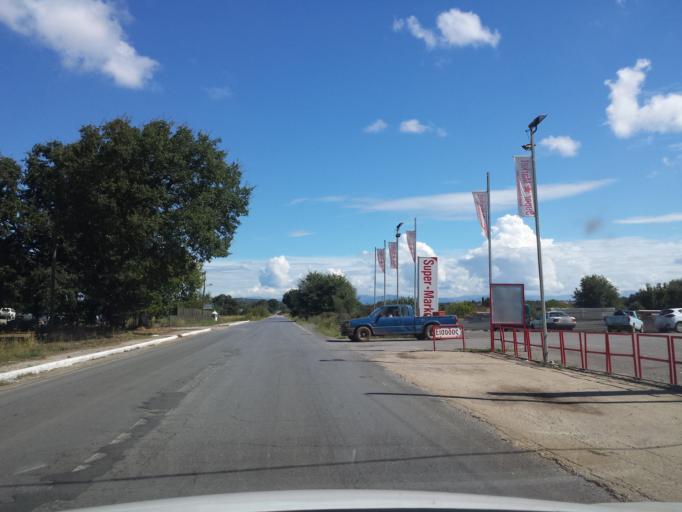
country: GR
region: Peloponnese
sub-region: Nomos Messinias
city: Vlakhopoulon
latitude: 36.9718
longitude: 21.8099
